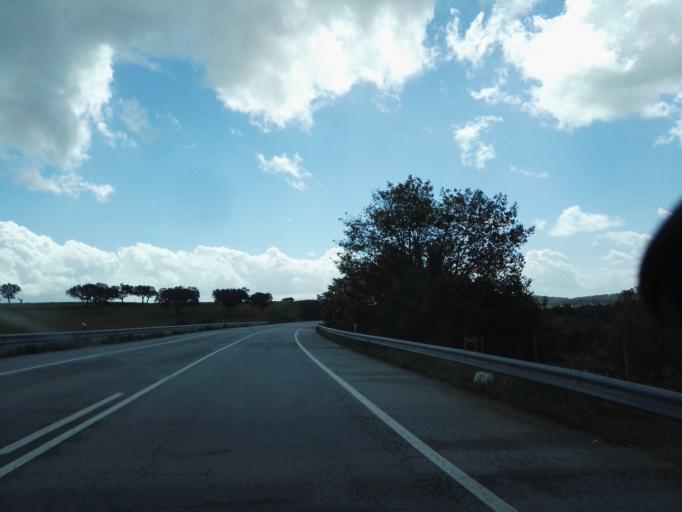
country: PT
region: Portalegre
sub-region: Portalegre
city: Urra
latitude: 39.2192
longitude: -7.3786
